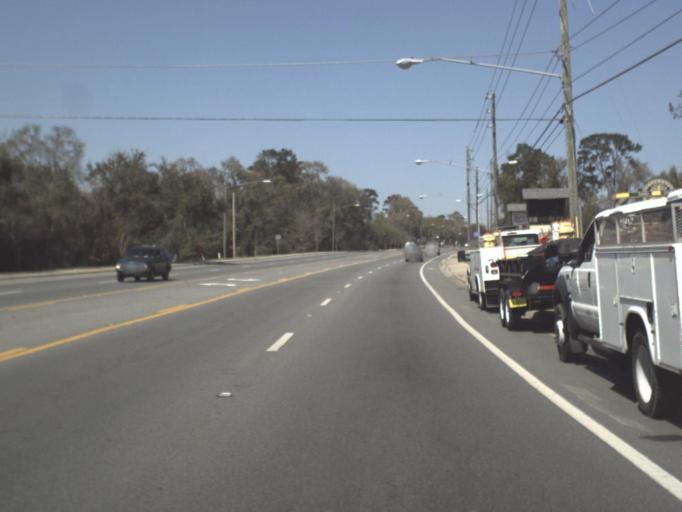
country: US
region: Florida
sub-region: Leon County
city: Tallahassee
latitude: 30.4000
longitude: -84.2804
